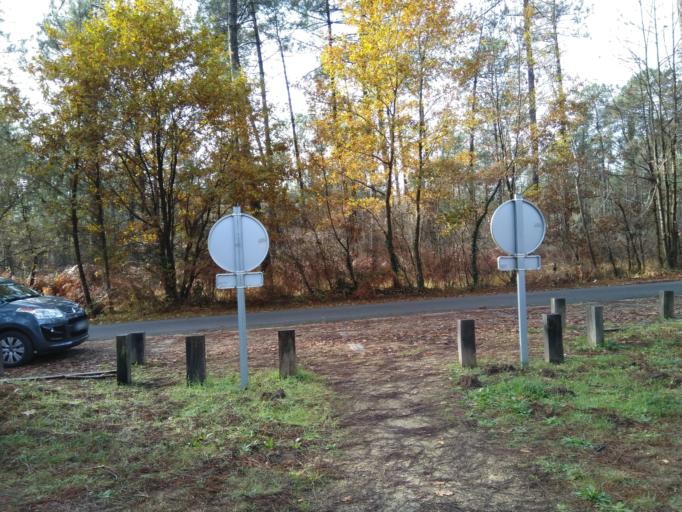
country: FR
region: Aquitaine
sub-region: Departement des Landes
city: Mees
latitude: 43.7045
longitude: -1.1260
